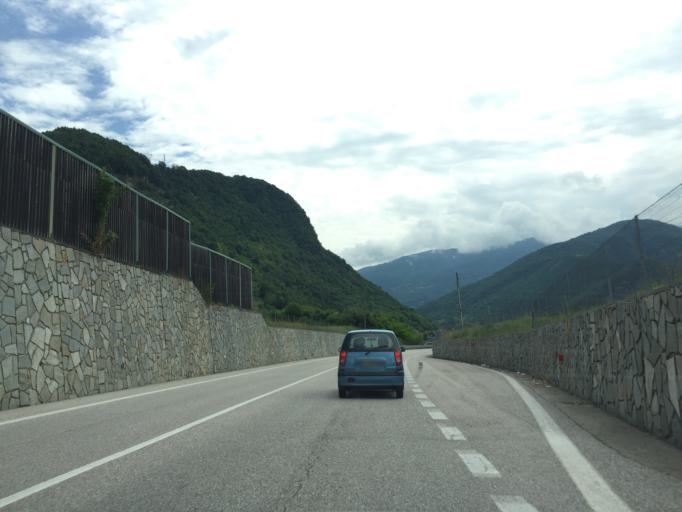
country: IT
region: Veneto
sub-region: Provincia di Belluno
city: Feltre
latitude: 46.0121
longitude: 11.9191
